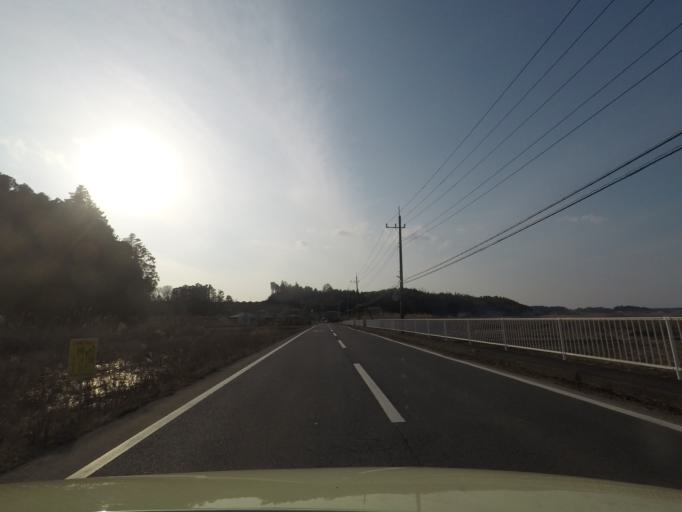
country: JP
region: Ibaraki
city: Okunoya
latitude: 36.2646
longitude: 140.4502
